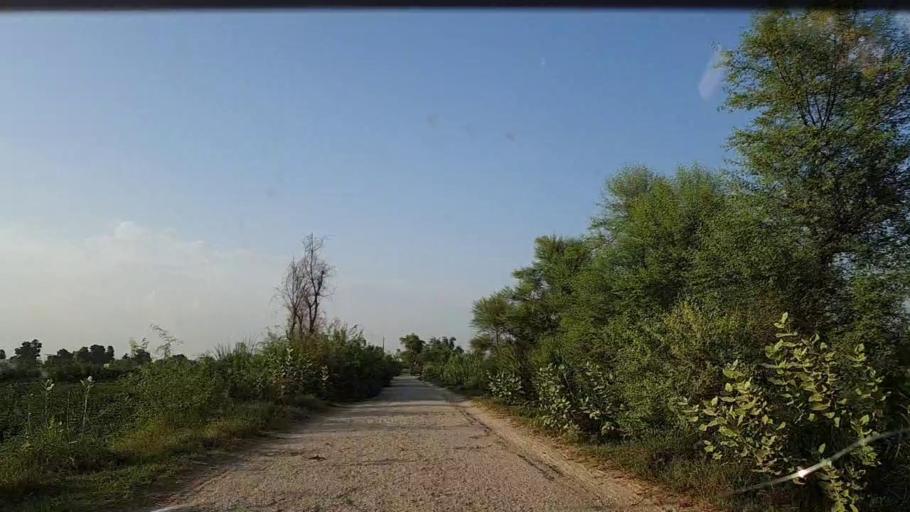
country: PK
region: Sindh
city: Pano Aqil
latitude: 27.9177
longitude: 69.2009
